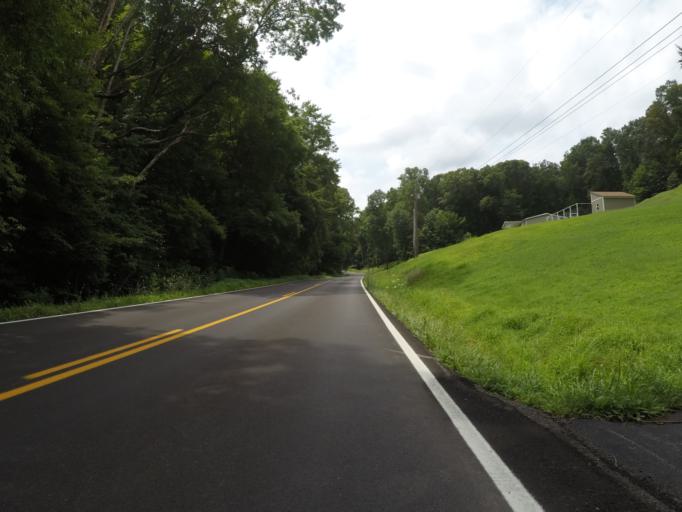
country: US
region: Kentucky
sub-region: Boyd County
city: Catlettsburg
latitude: 38.4334
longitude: -82.6283
